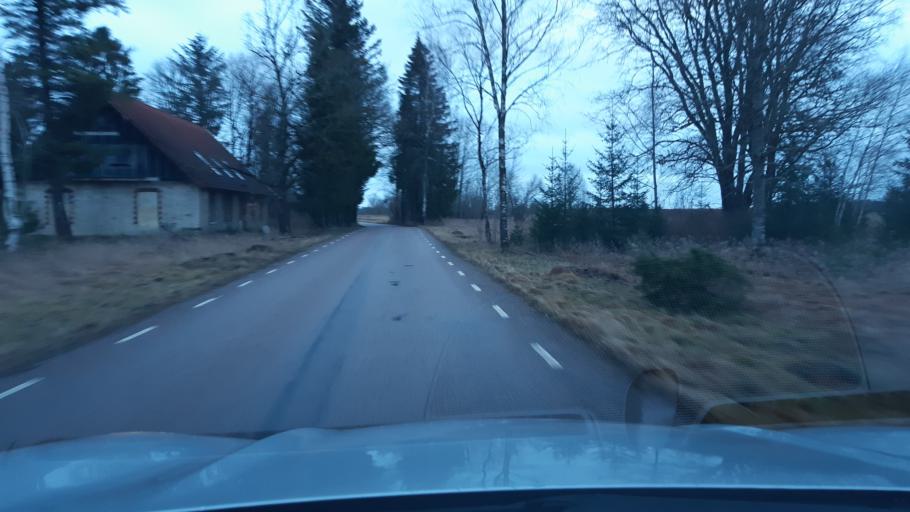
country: EE
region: Raplamaa
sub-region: Rapla vald
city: Rapla
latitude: 58.9971
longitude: 24.7185
